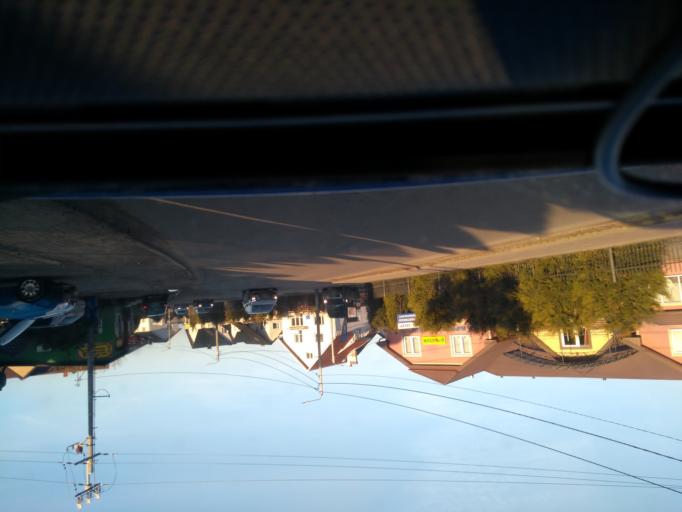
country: PL
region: Pomeranian Voivodeship
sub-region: Powiat kartuski
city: Przodkowo
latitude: 54.4142
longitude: 18.3180
